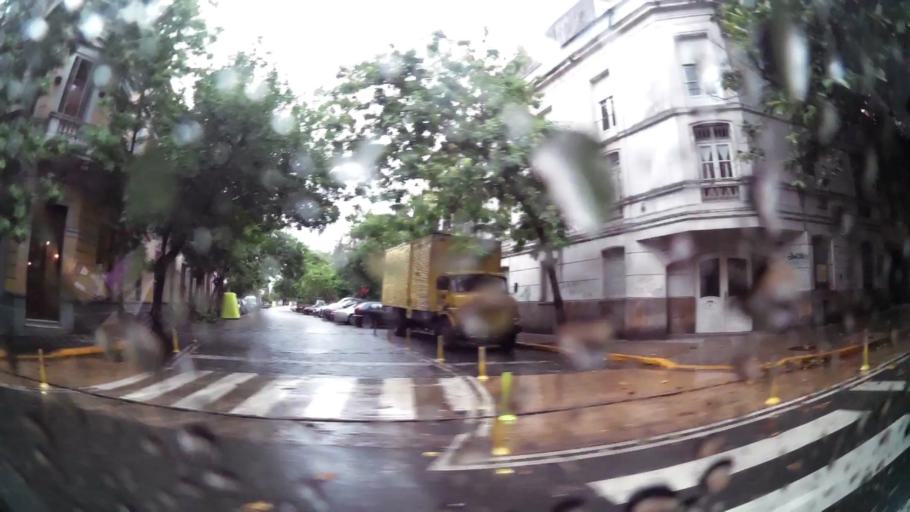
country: AR
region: Buenos Aires F.D.
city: Buenos Aires
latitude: -34.6278
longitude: -58.3726
